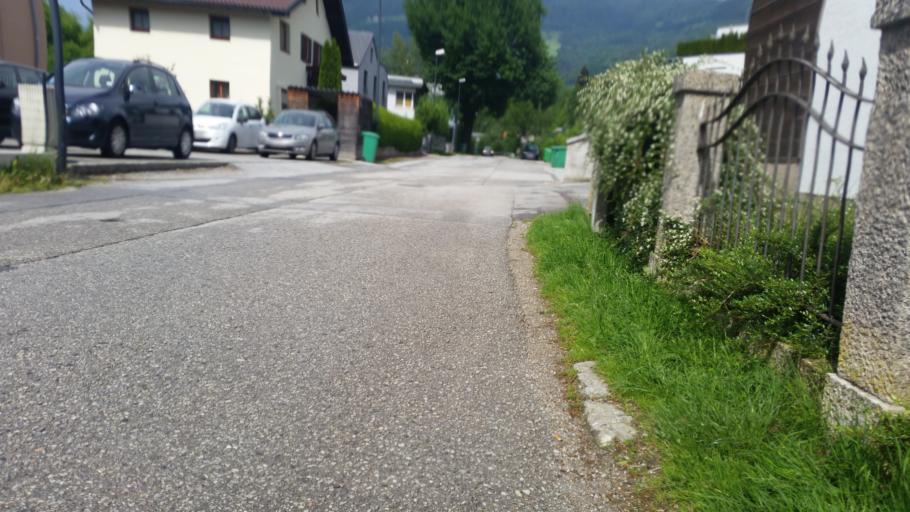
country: AT
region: Salzburg
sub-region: Politischer Bezirk Salzburg-Umgebung
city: Elsbethen
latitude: 47.7770
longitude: 13.0792
